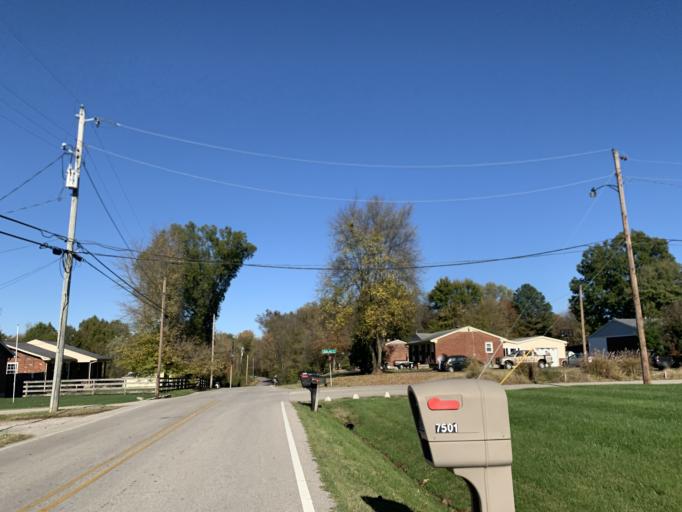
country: US
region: Kentucky
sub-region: Jefferson County
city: Pleasure Ridge Park
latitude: 38.1471
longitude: -85.8809
